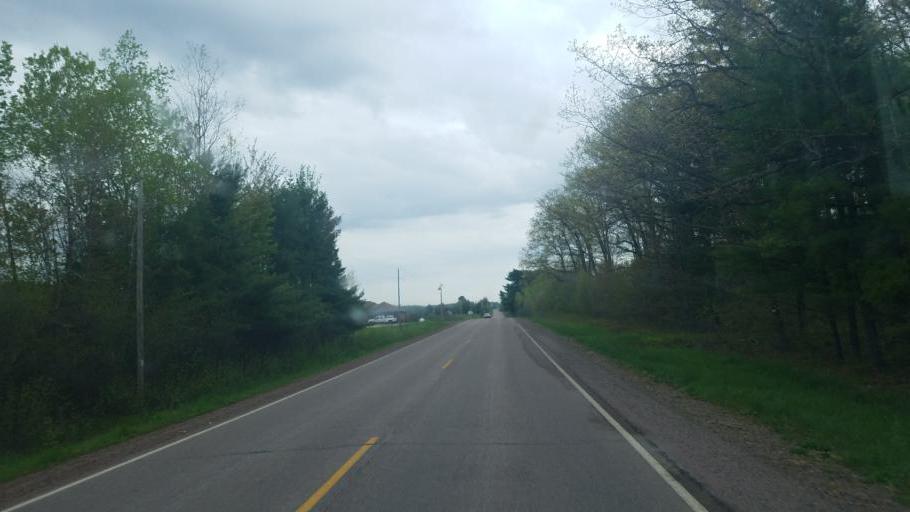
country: US
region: Wisconsin
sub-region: Wood County
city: Marshfield
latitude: 44.5646
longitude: -90.2999
